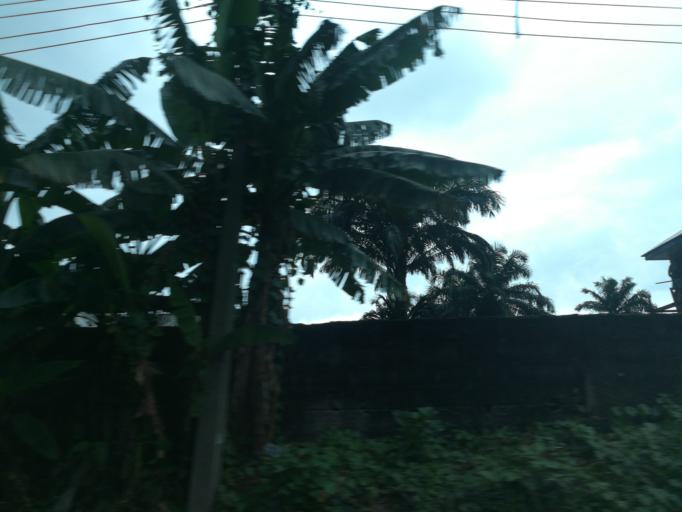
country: NG
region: Rivers
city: Port Harcourt
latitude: 4.8033
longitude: 6.9877
